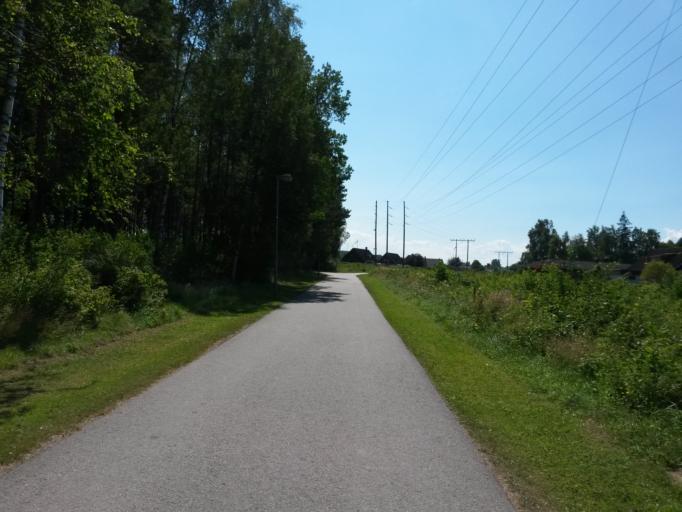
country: SE
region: Vaestra Goetaland
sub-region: Lidkopings Kommun
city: Lidkoping
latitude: 58.4856
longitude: 13.1478
